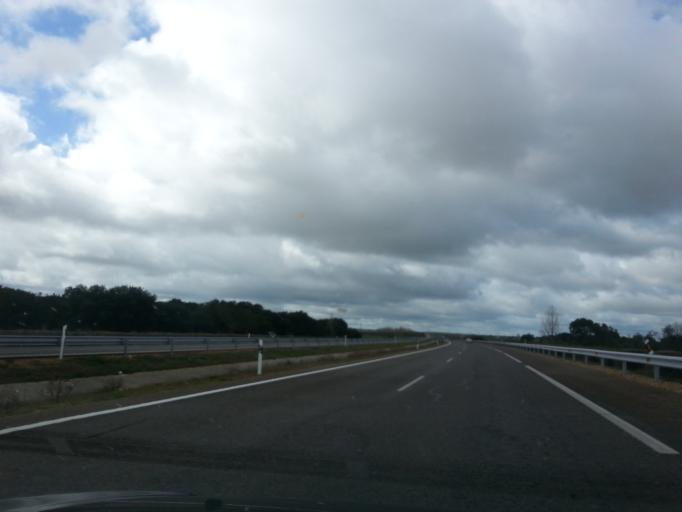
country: ES
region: Castille and Leon
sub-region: Provincia de Salamanca
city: La Fuente de San Esteban
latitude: 40.8015
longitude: -6.2037
